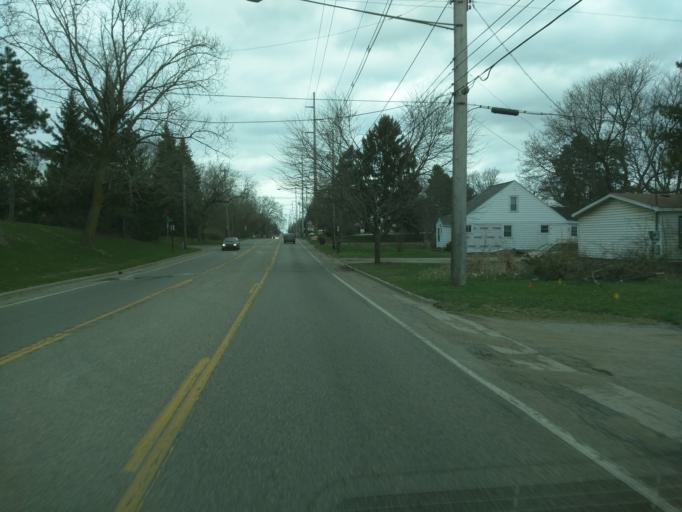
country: US
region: Michigan
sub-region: Ingham County
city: Lansing
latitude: 42.6963
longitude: -84.5234
